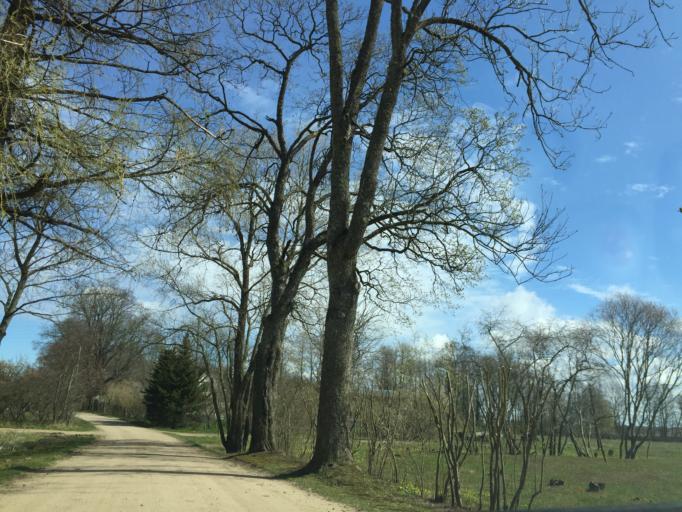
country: LV
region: Salacgrivas
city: Salacgriva
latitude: 57.6978
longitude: 24.3623
